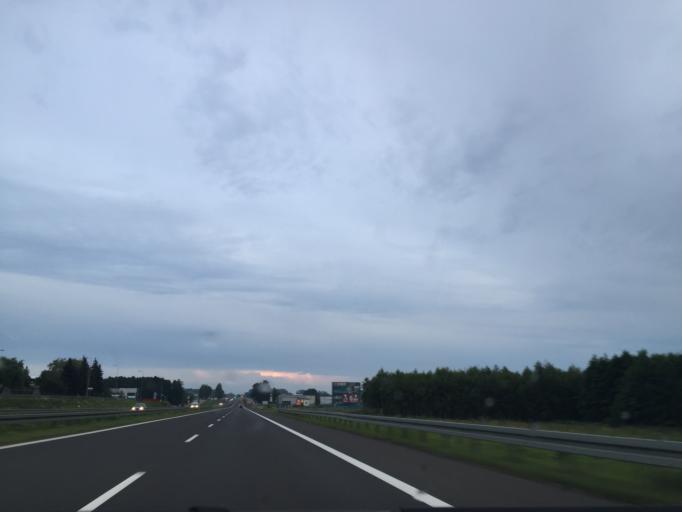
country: PL
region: Podlasie
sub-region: Powiat bialostocki
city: Choroszcz
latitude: 53.1547
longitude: 23.0243
